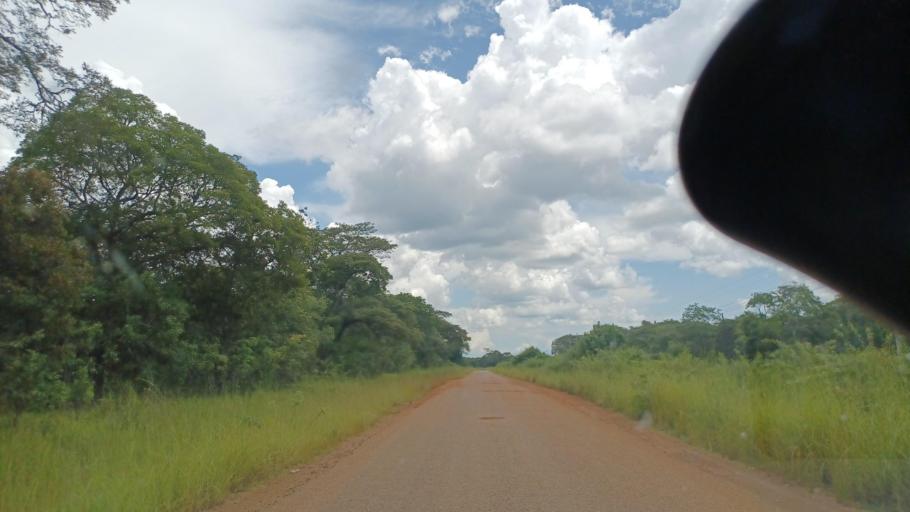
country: ZM
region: North-Western
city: Solwezi
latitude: -12.7134
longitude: 26.0239
